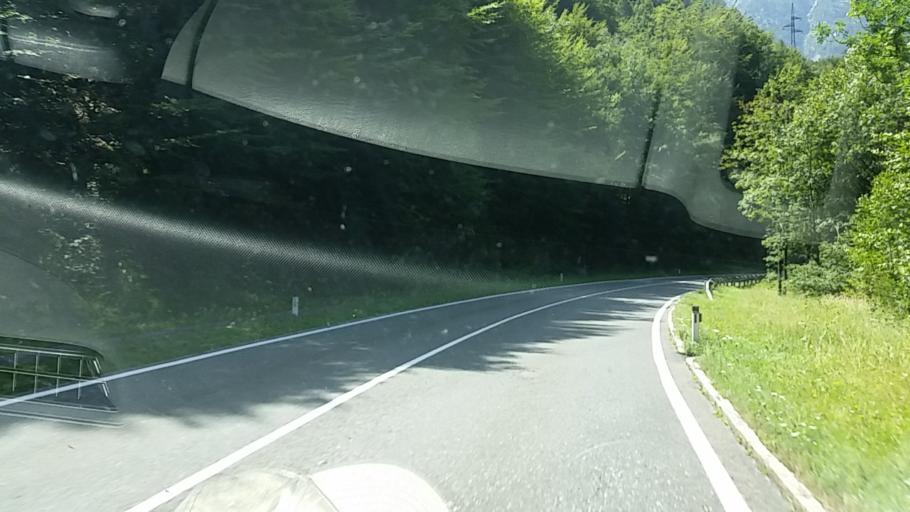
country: AT
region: Salzburg
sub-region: Politischer Bezirk Hallein
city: Scheffau am Tennengebirge
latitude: 47.5734
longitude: 13.1946
